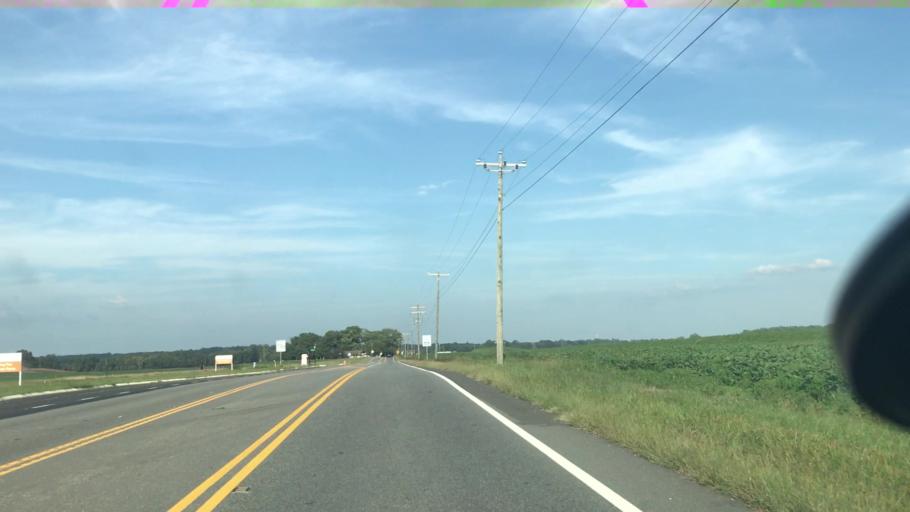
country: US
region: Virginia
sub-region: City of Fredericksburg
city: Fredericksburg
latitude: 38.2351
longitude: -77.4001
